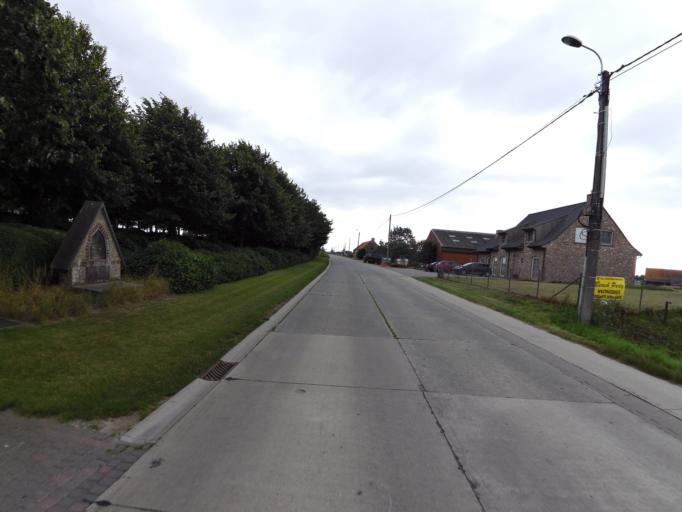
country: BE
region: Flanders
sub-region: Provincie West-Vlaanderen
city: Kortemark
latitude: 51.0083
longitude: 3.0437
